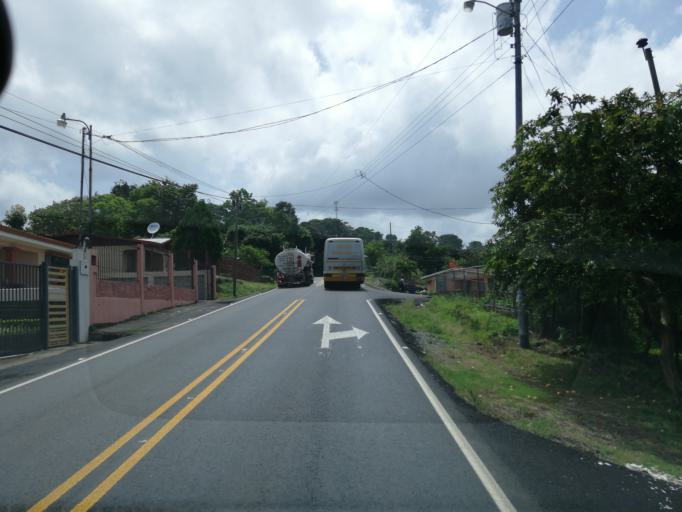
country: CR
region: Alajuela
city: Naranjo
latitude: 10.1308
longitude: -84.3998
